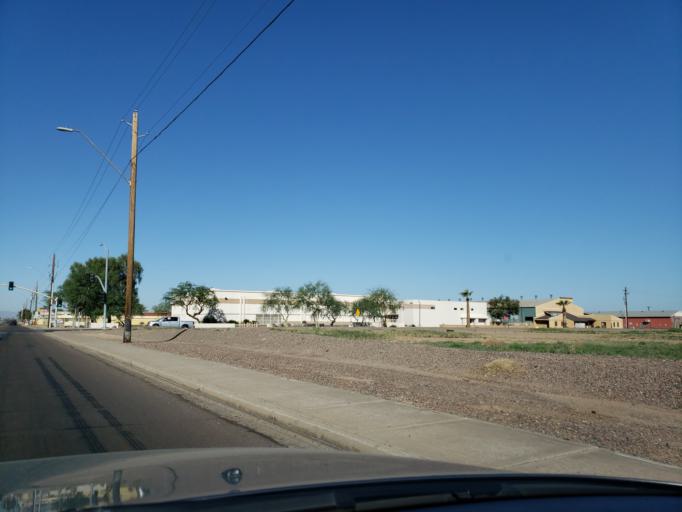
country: US
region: Arizona
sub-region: Maricopa County
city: Glendale
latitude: 33.5241
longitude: -112.1766
